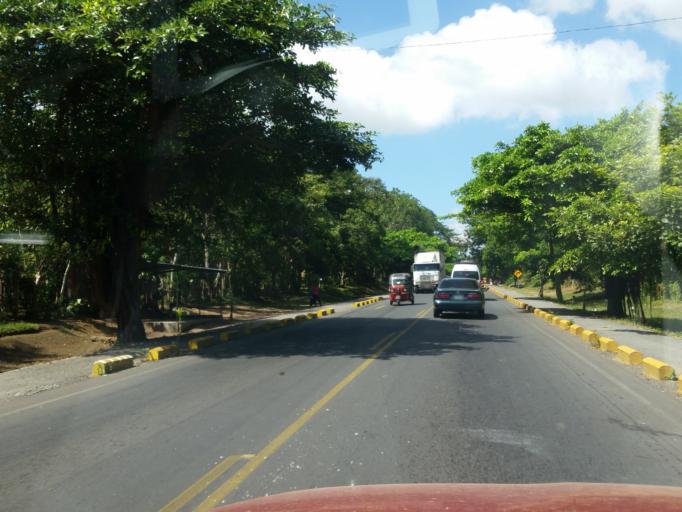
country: NI
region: Granada
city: Diriomo
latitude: 11.8548
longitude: -86.0249
